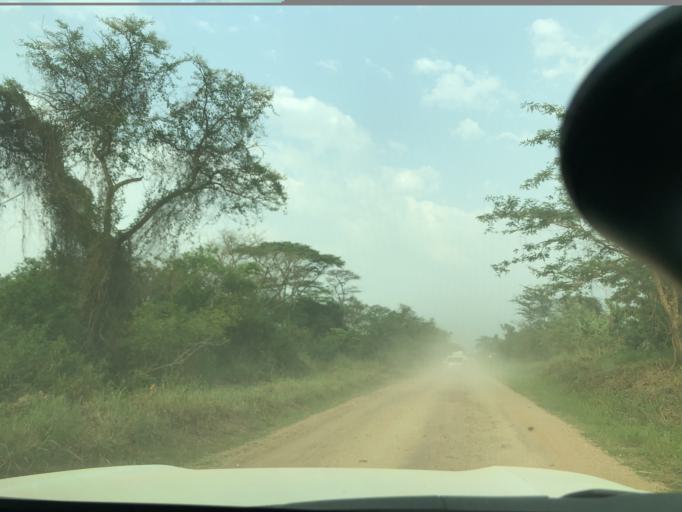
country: UG
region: Western Region
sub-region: Kasese District
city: Margherita
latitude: 0.1992
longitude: 29.6659
